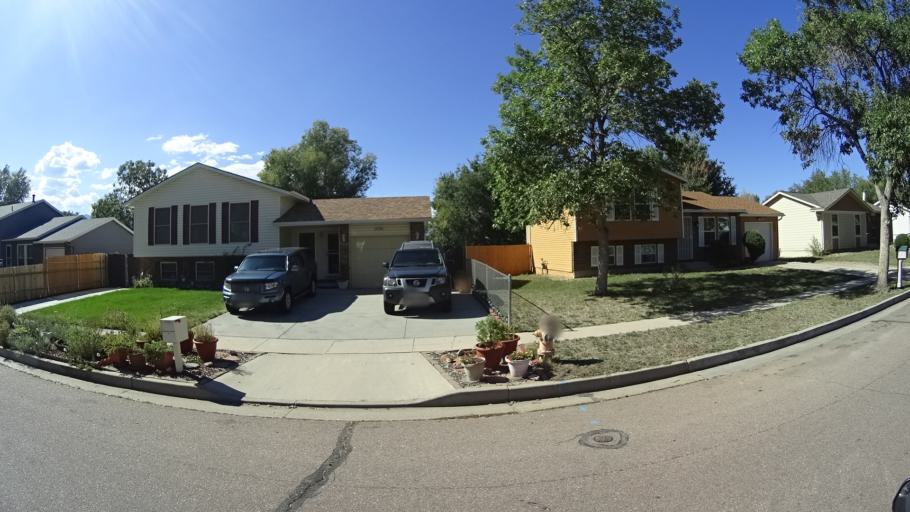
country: US
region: Colorado
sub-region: El Paso County
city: Stratmoor
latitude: 38.7920
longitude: -104.7475
